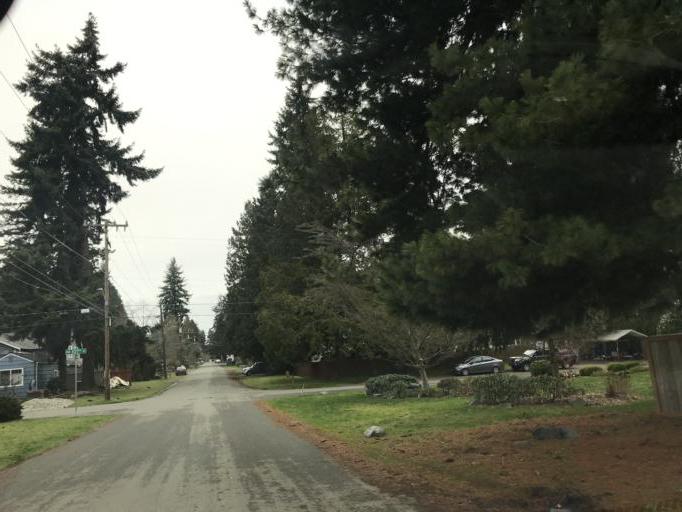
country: US
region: Washington
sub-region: King County
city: Lake Forest Park
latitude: 47.7062
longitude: -122.3062
